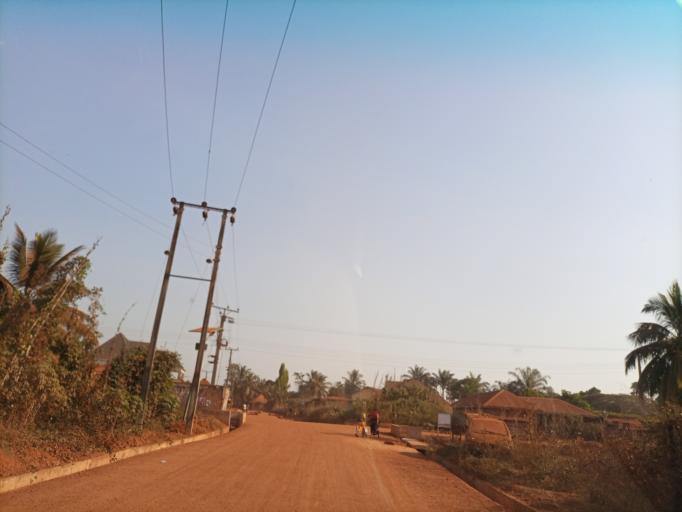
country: NG
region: Enugu
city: Opi
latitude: 6.7494
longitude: 7.4097
